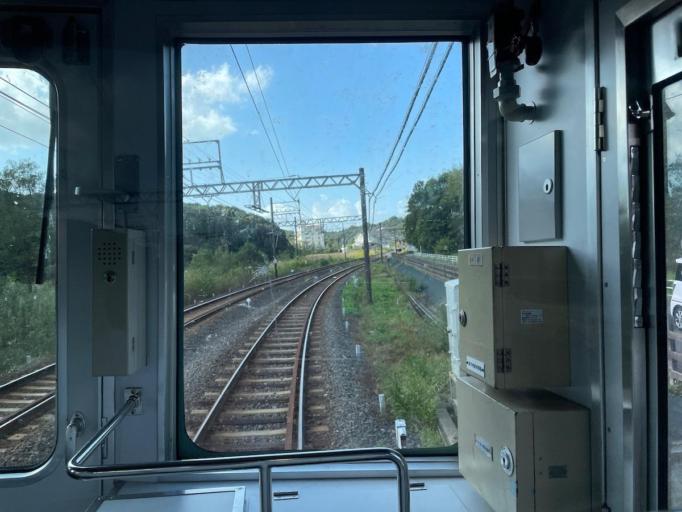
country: JP
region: Mie
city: Toba
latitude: 34.3183
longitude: 136.8313
